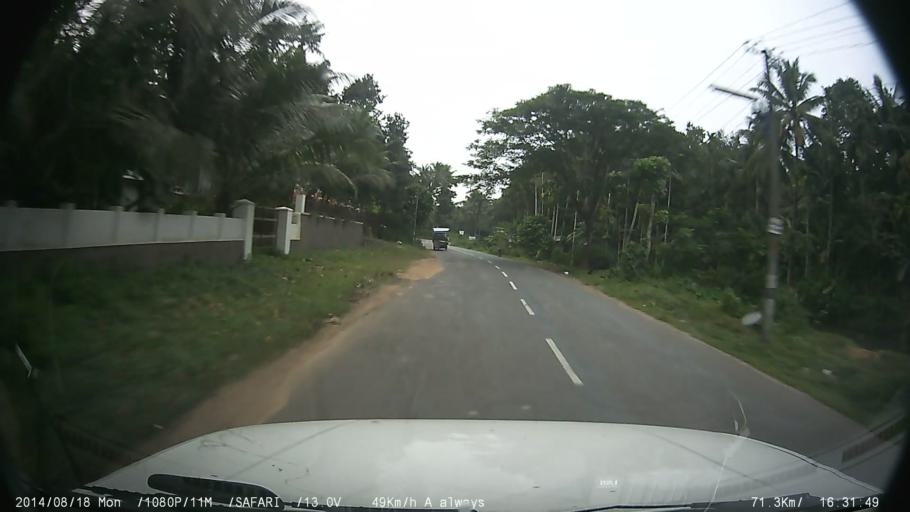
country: IN
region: Kerala
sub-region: Kottayam
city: Palackattumala
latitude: 9.7990
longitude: 76.5741
